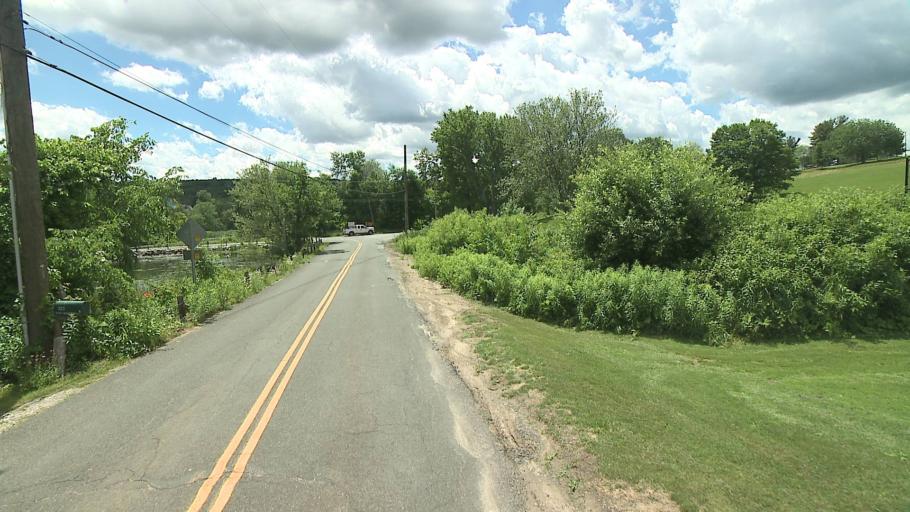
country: US
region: Connecticut
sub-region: Litchfield County
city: New Preston
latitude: 41.6966
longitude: -73.3781
